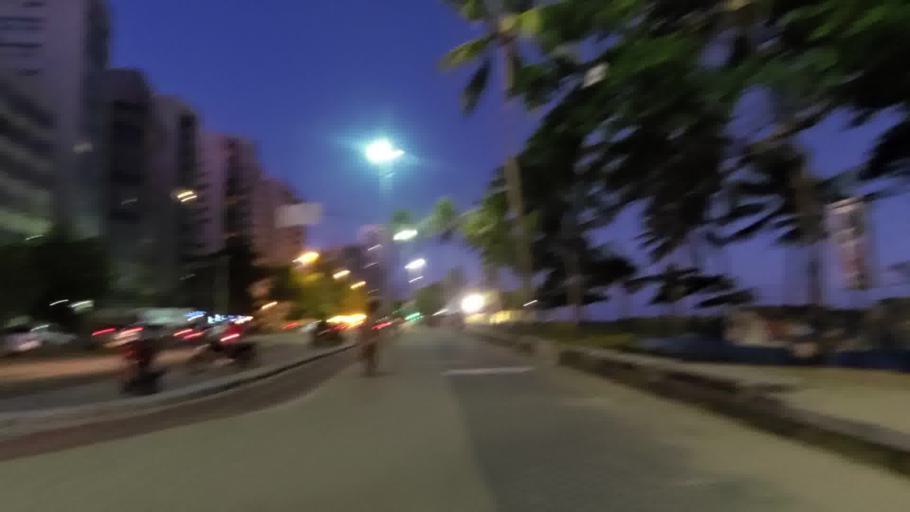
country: BR
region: Pernambuco
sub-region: Recife
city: Recife
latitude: -8.1031
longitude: -34.8859
